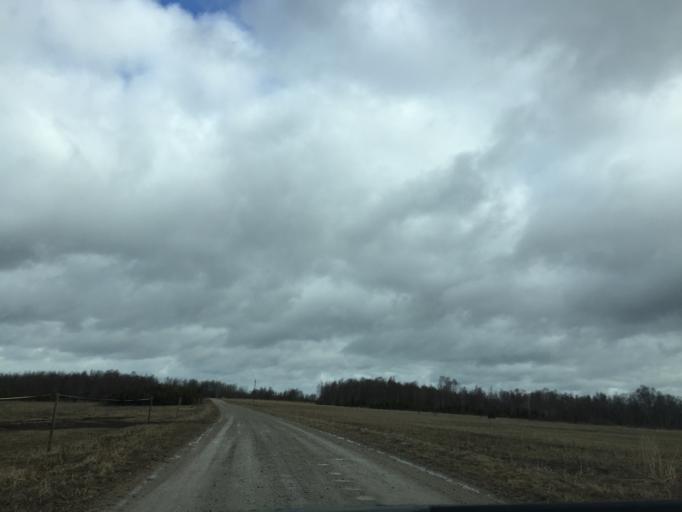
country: EE
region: Laeaene
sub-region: Haapsalu linn
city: Haapsalu
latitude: 58.6796
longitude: 23.5420
